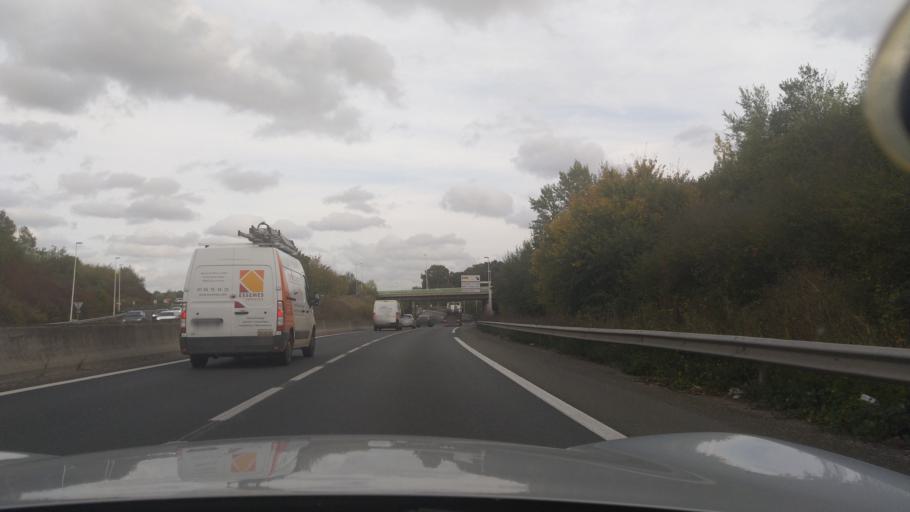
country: FR
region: Ile-de-France
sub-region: Departement du Val-d'Oise
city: Mery-sur-Oise
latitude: 49.0515
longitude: 2.1837
